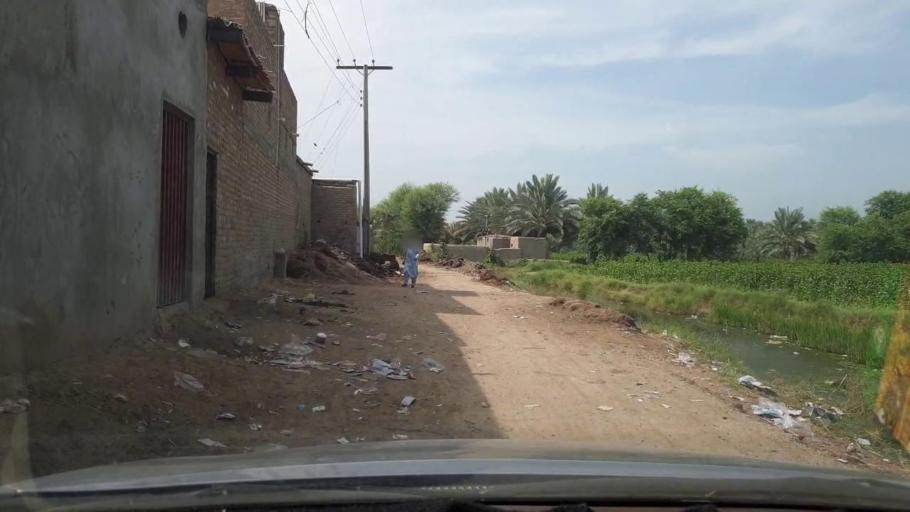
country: PK
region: Sindh
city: Khairpur
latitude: 27.4988
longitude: 68.7546
